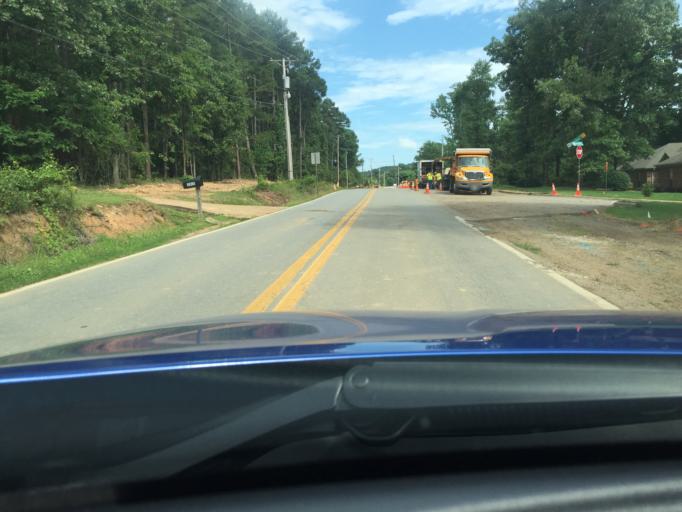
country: US
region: Arkansas
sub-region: Pulaski County
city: Maumelle
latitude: 34.8071
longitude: -92.4387
